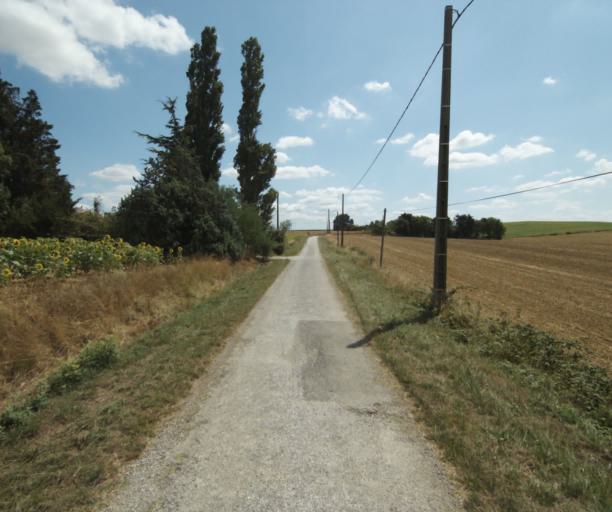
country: FR
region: Midi-Pyrenees
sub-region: Departement de la Haute-Garonne
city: Auriac-sur-Vendinelle
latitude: 43.4682
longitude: 1.8308
